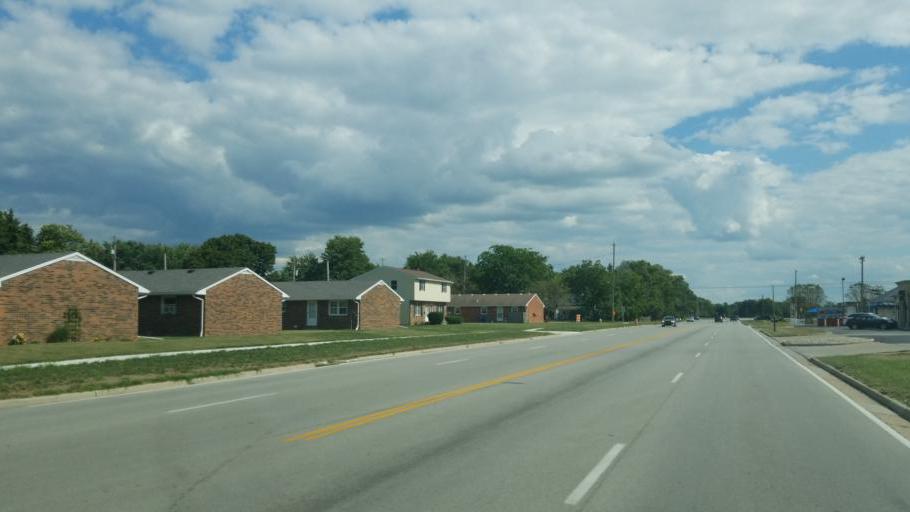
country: US
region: Ohio
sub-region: Wood County
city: Perrysburg
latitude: 41.5494
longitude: -83.6374
